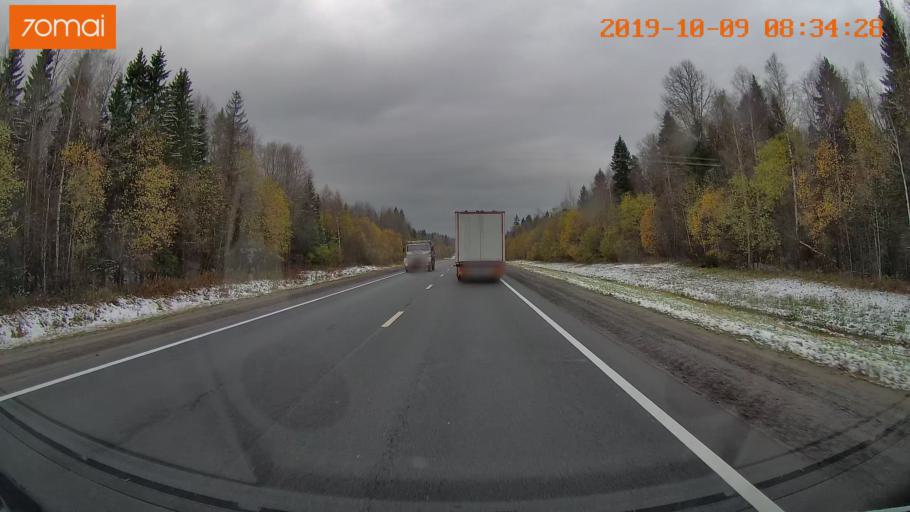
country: RU
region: Vologda
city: Gryazovets
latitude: 58.8971
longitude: 40.1854
